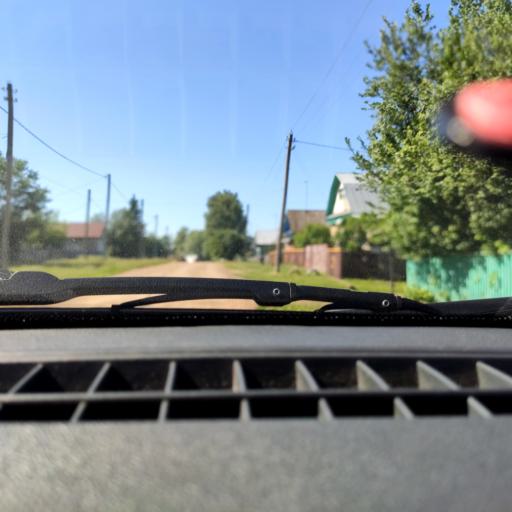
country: RU
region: Bashkortostan
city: Iglino
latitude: 54.8948
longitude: 56.4954
